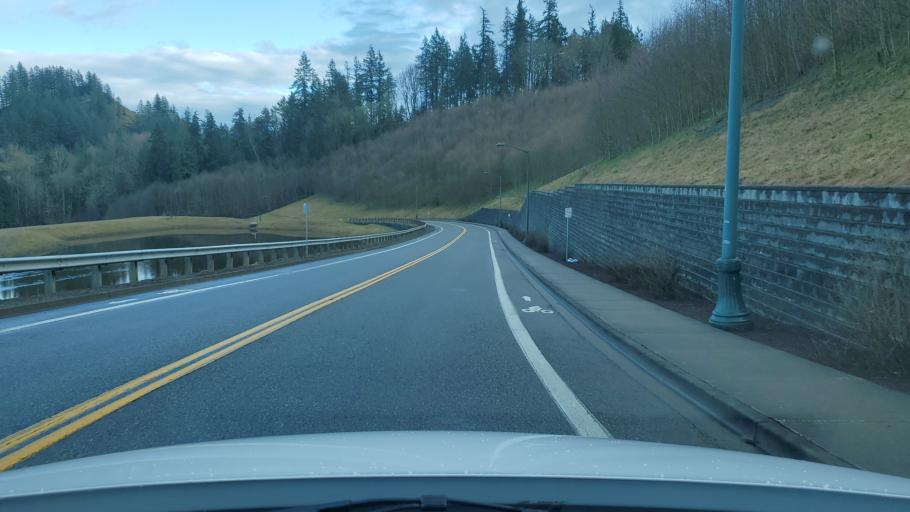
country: US
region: Washington
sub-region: Skagit County
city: Big Lake
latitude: 48.4299
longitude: -122.2720
